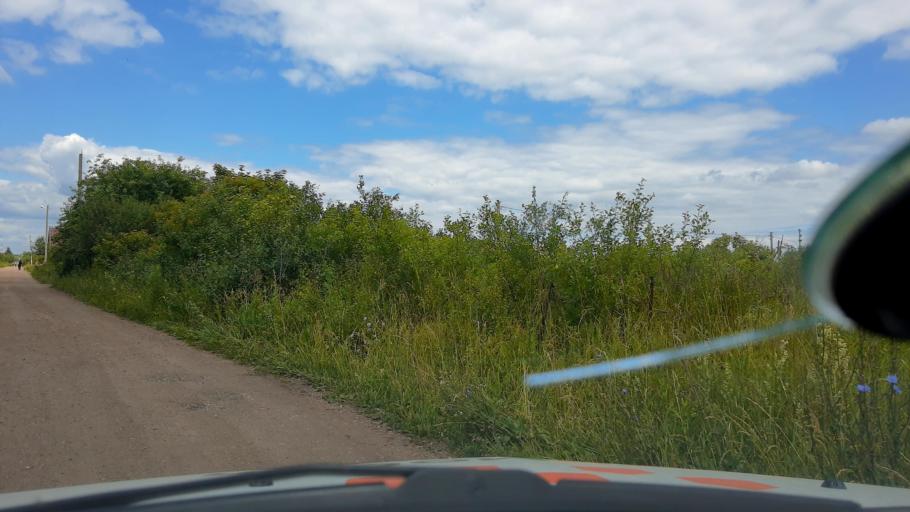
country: RU
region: Bashkortostan
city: Kabakovo
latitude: 54.7200
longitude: 56.2095
